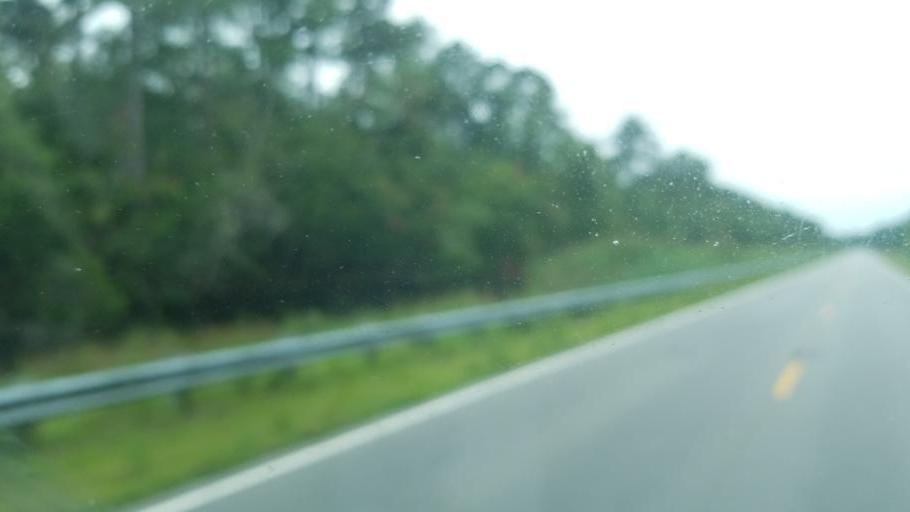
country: US
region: North Carolina
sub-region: Tyrrell County
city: Columbia
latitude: 35.9274
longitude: -76.1401
